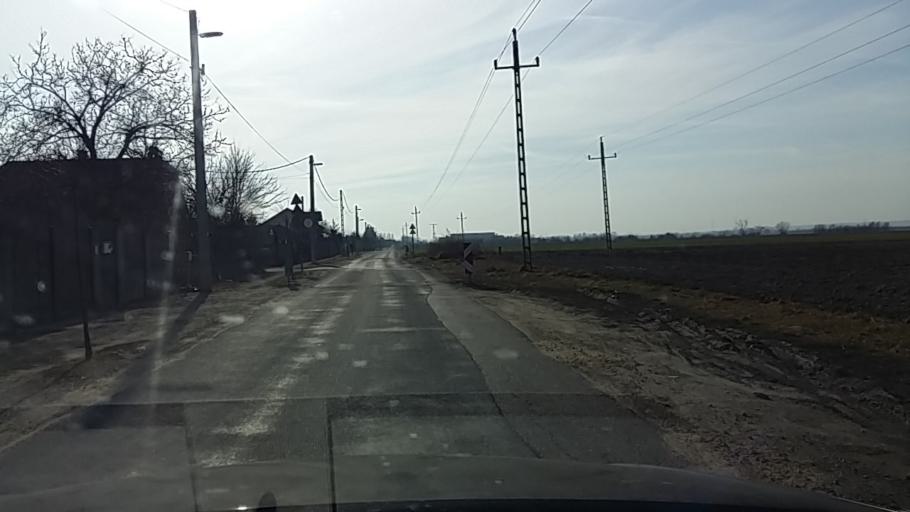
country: HU
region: Pest
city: Szigetszentmiklos
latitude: 47.3568
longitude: 19.0271
